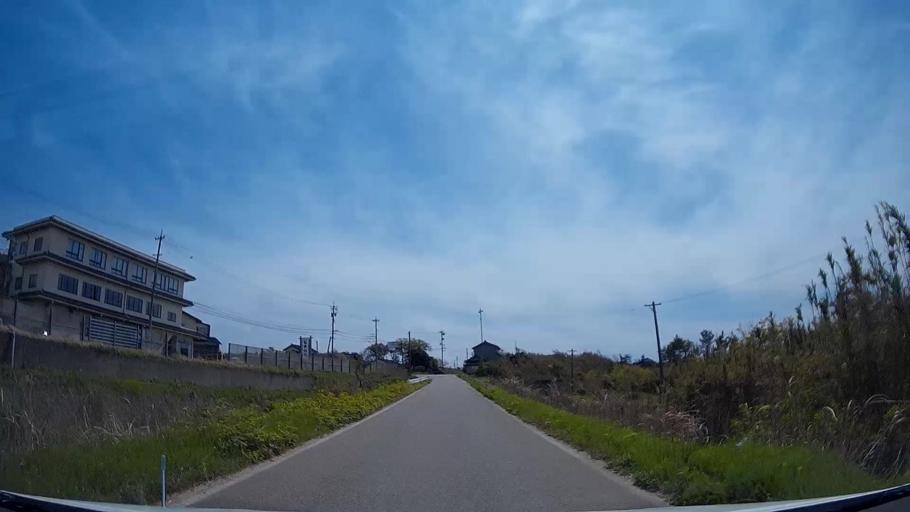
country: JP
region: Ishikawa
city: Hakui
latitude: 36.9458
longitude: 136.7634
